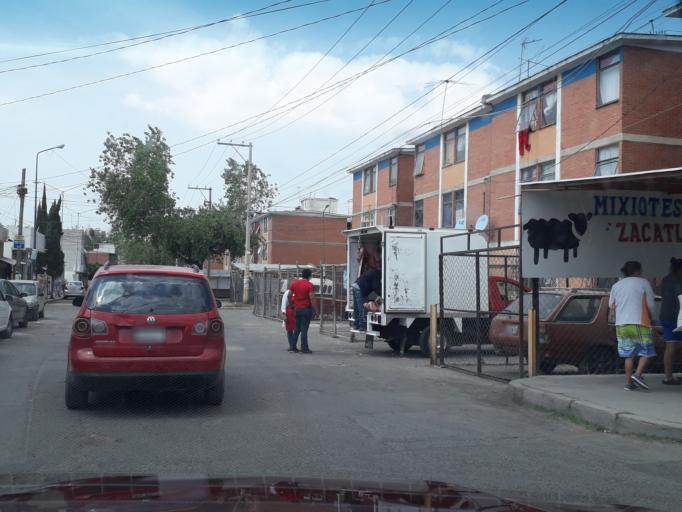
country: MX
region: Puebla
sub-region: Puebla
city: El Capulo (La Quebradora)
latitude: 18.9694
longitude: -98.2609
